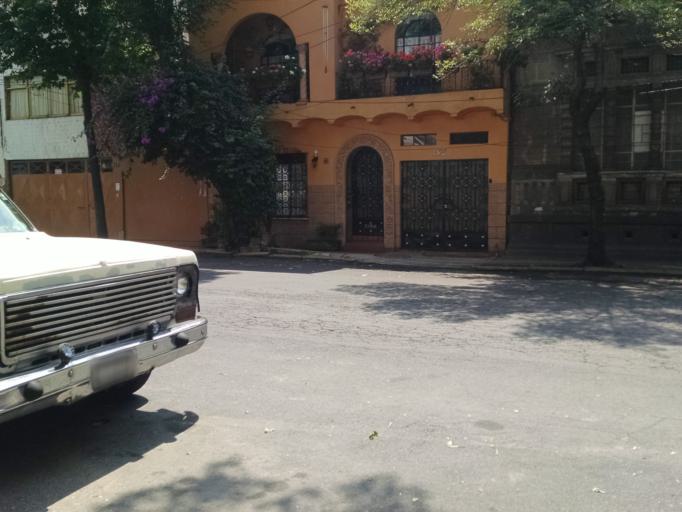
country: MX
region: Mexico City
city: Cuauhtemoc
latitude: 19.4481
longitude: -99.1580
